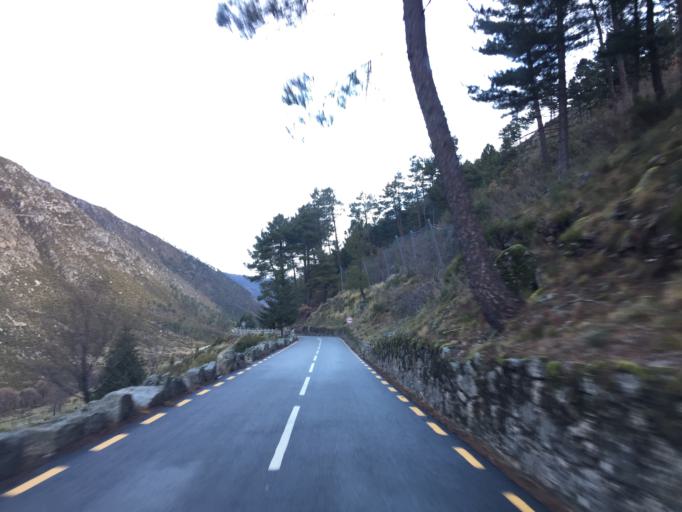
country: PT
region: Guarda
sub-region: Manteigas
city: Manteigas
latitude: 40.3493
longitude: -7.5604
